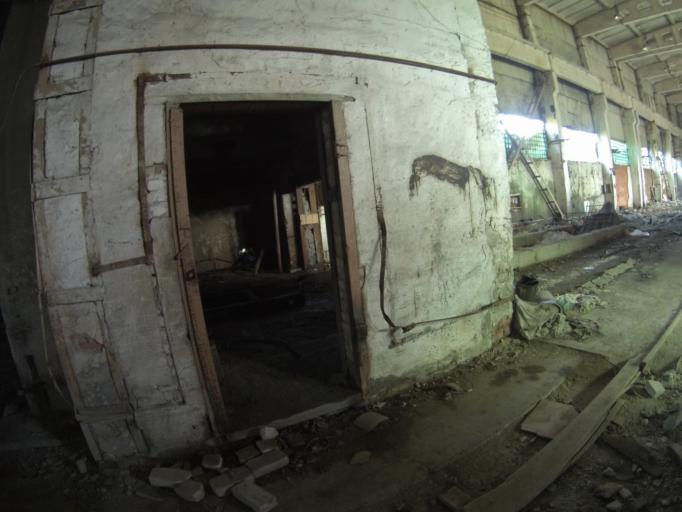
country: RU
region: Vladimir
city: Raduzhnyy
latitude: 55.9778
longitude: 40.2677
